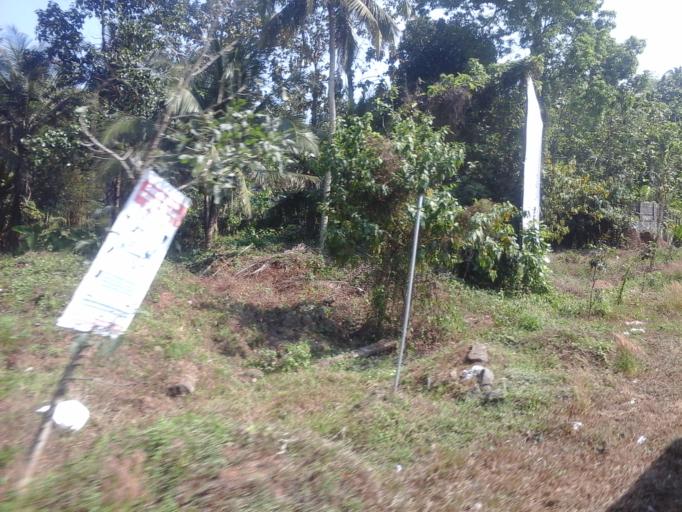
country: IN
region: Kerala
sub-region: Kottayam
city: Erattupetta
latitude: 9.7021
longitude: 76.7538
